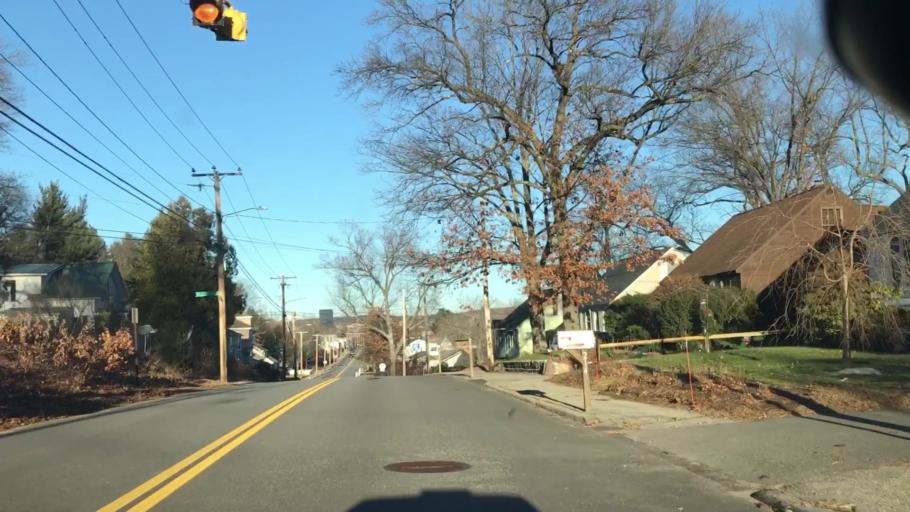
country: US
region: New Hampshire
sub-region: Hillsborough County
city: Pinardville
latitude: 42.9707
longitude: -71.4858
